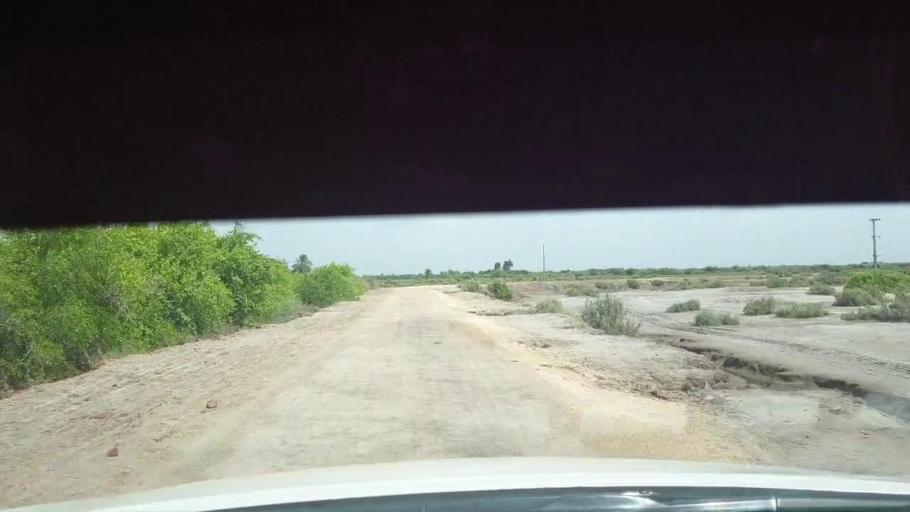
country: PK
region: Sindh
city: Kadhan
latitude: 24.5194
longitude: 68.9700
